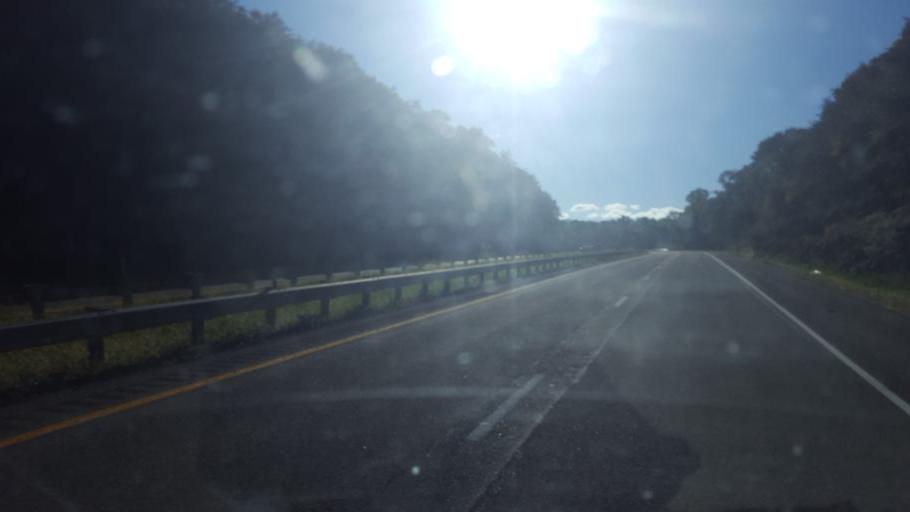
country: US
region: West Virginia
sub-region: Morgan County
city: Berkeley Springs
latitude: 39.6655
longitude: -78.4270
